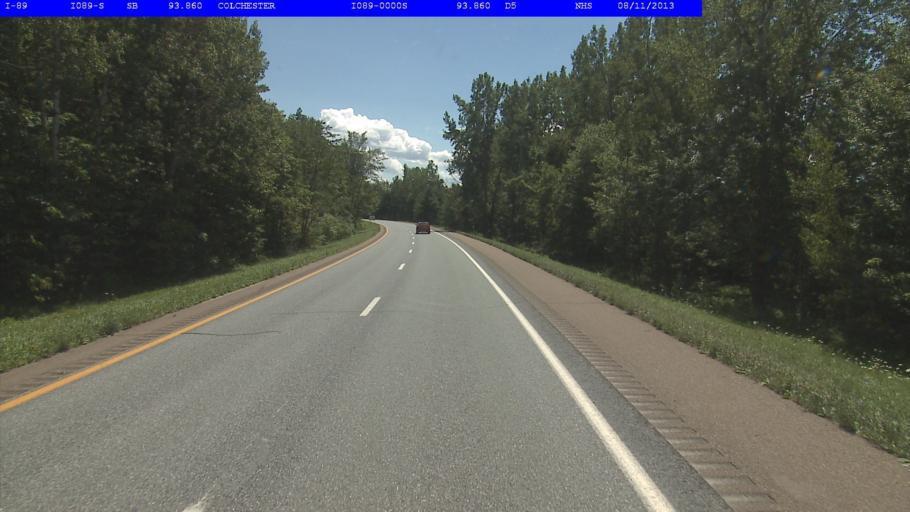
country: US
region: Vermont
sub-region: Chittenden County
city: Winooski
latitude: 44.5363
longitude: -73.1992
